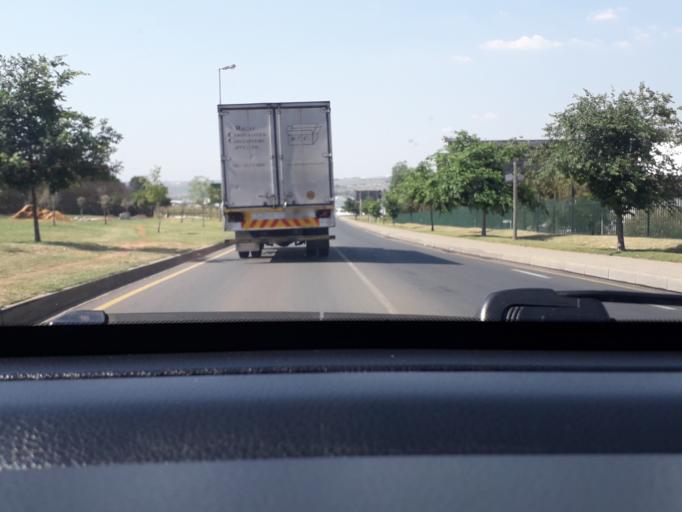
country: ZA
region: Gauteng
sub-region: City of Johannesburg Metropolitan Municipality
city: Modderfontein
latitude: -26.1071
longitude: 28.1371
